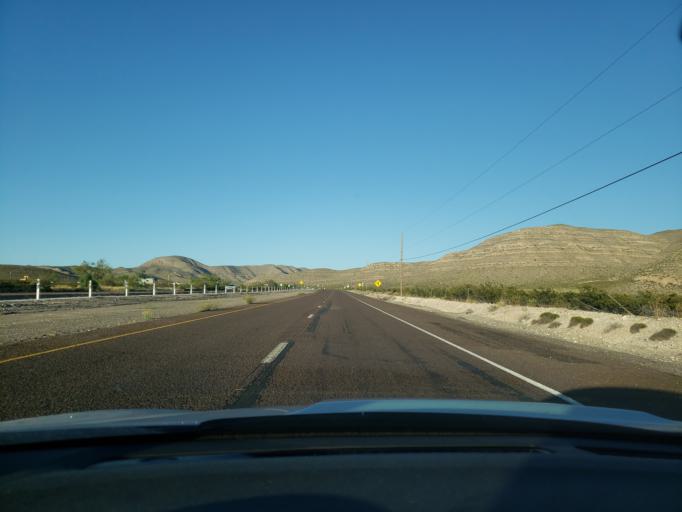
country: US
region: Texas
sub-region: El Paso County
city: Homestead Meadows South
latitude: 31.8329
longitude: -106.0687
